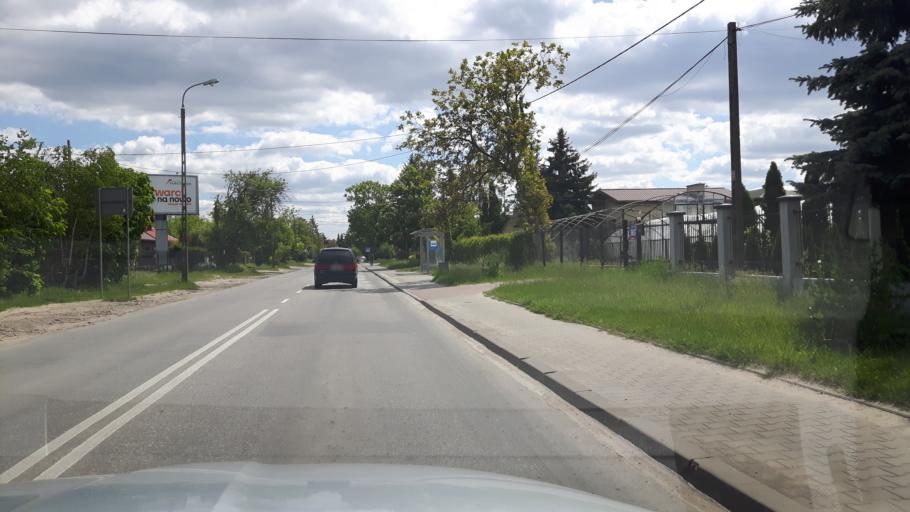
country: PL
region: Masovian Voivodeship
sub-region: Warszawa
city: Targowek
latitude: 52.3258
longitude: 21.0318
